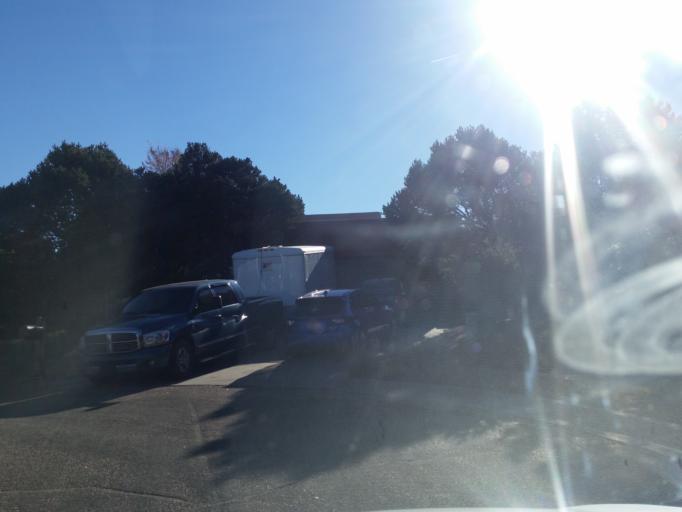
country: US
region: New Mexico
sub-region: Santa Fe County
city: Santa Fe
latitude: 35.6494
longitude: -105.9308
